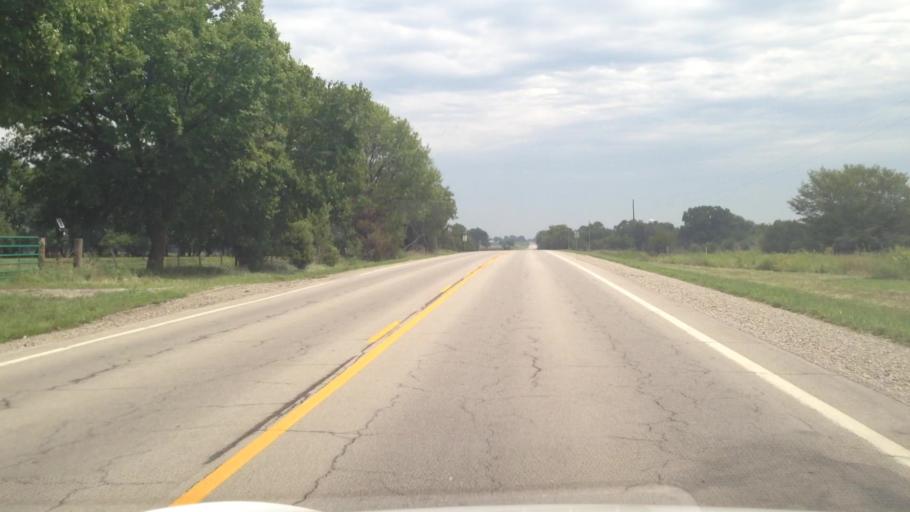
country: US
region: Kansas
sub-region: Crawford County
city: Girard
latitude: 37.5143
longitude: -94.8926
